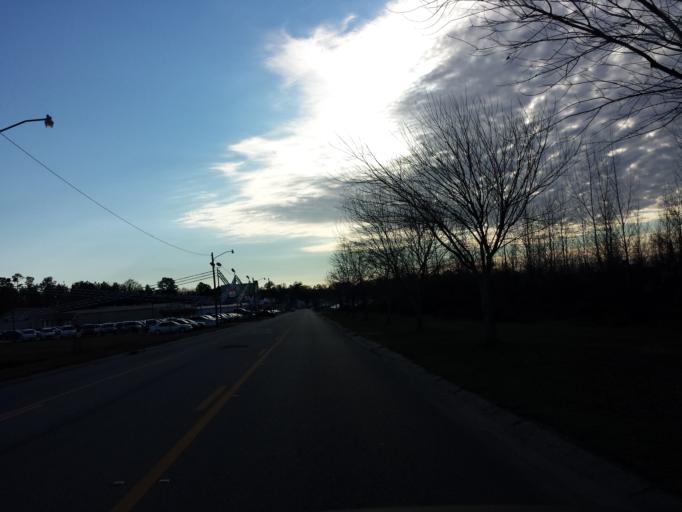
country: US
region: Mississippi
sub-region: Forrest County
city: Hattiesburg
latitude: 31.3086
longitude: -89.3108
